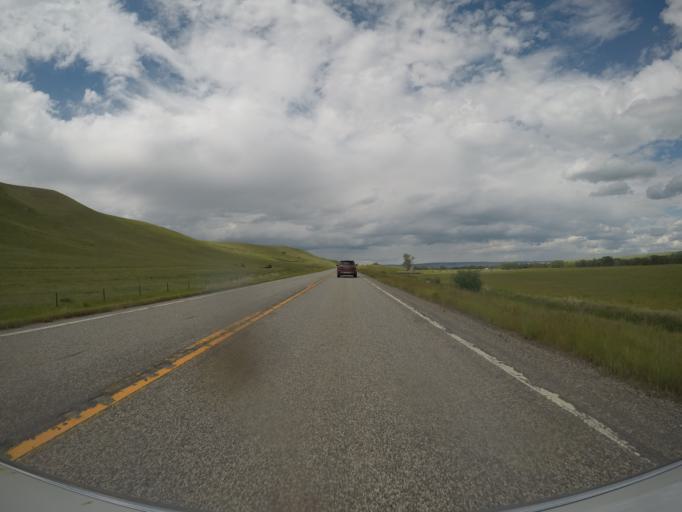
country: US
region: Montana
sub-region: Sweet Grass County
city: Big Timber
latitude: 45.7981
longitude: -109.9701
